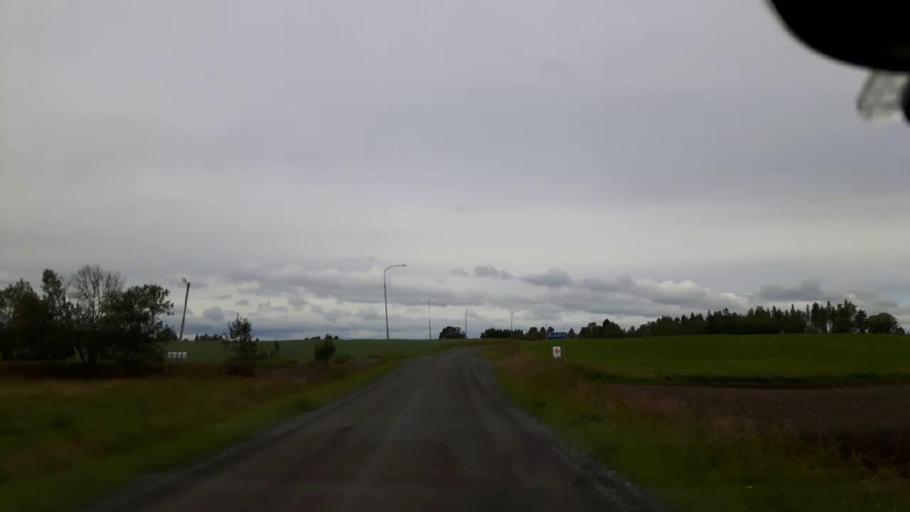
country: SE
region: Jaemtland
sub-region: Krokoms Kommun
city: Krokom
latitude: 63.3065
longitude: 14.3372
